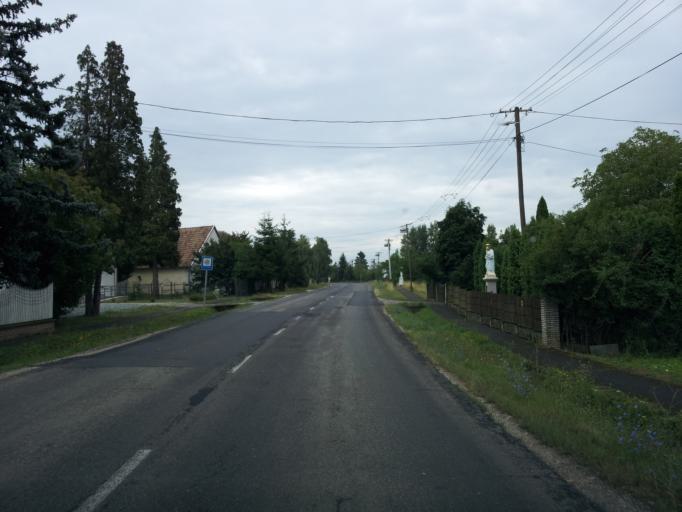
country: HU
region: Vas
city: Kormend
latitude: 46.9579
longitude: 16.6432
